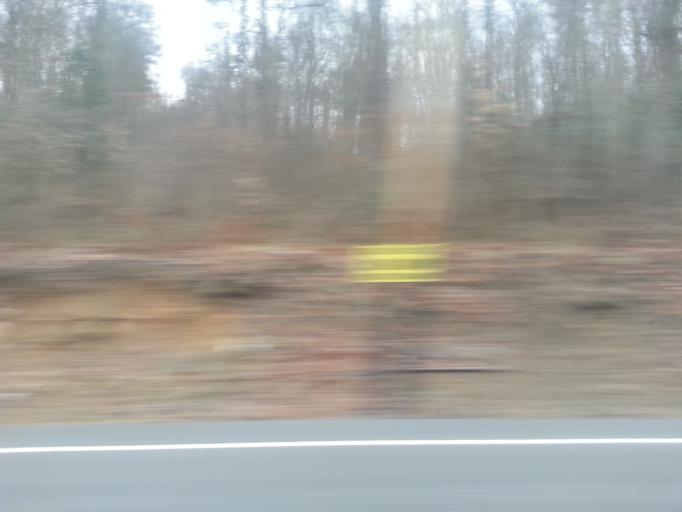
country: US
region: Tennessee
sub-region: Roane County
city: Harriman
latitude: 36.0204
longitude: -84.5265
